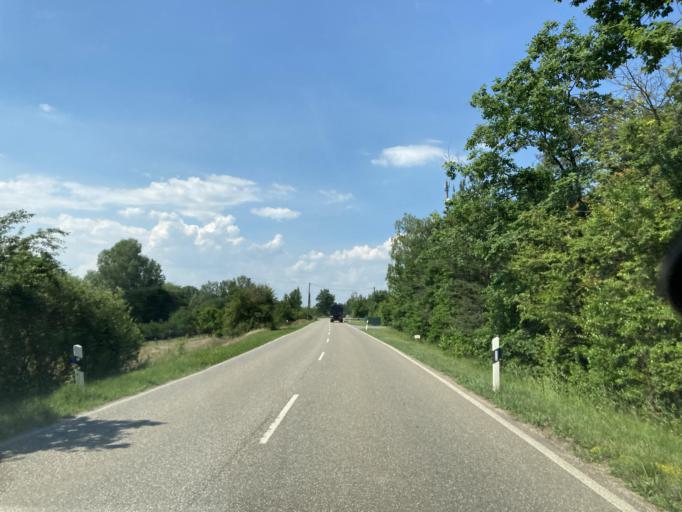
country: DE
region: Baden-Wuerttemberg
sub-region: Karlsruhe Region
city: Graben-Neudorf
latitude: 49.1847
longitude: 8.4847
